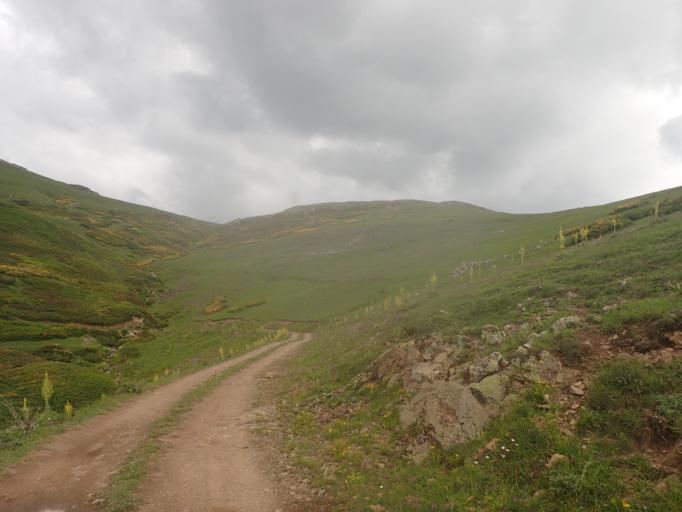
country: TR
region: Ordu
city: Yesilce
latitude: 40.5952
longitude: 37.9563
